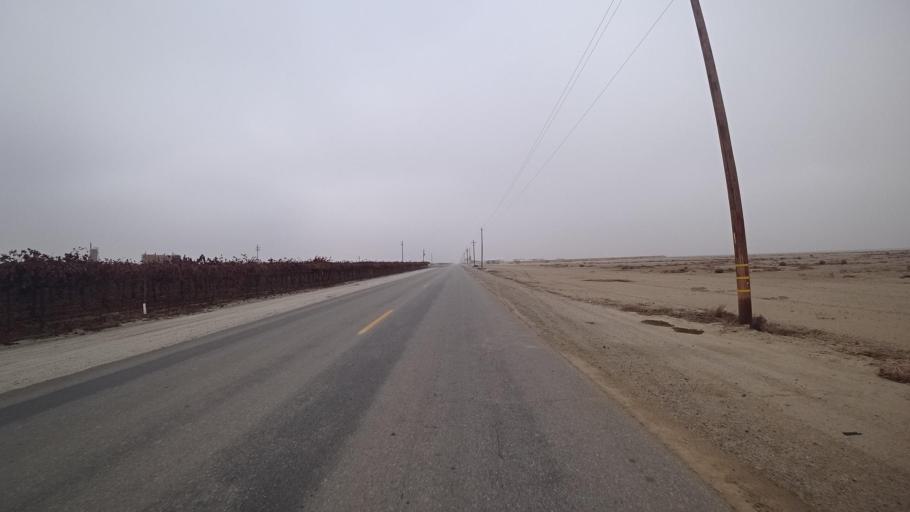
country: US
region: California
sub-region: Kern County
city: Greenfield
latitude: 35.0944
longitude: -119.1345
